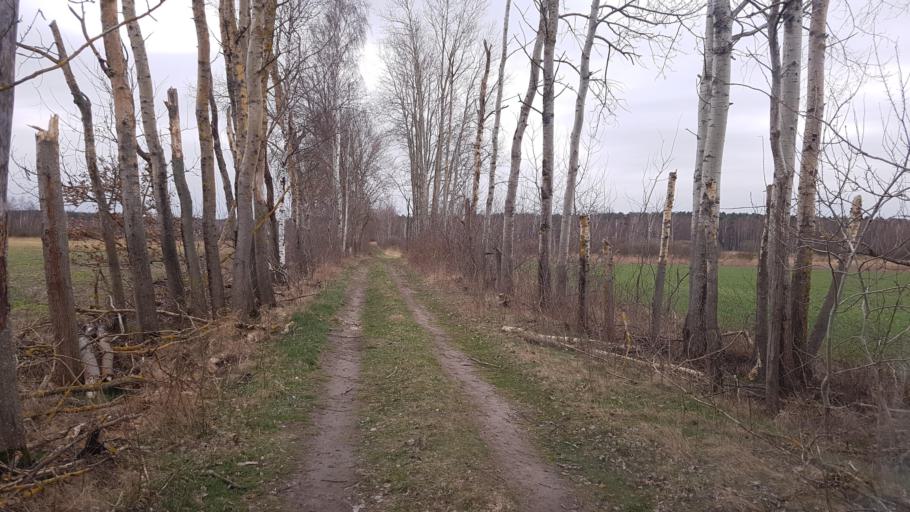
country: DE
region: Brandenburg
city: Hohenleipisch
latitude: 51.5324
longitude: 13.6044
